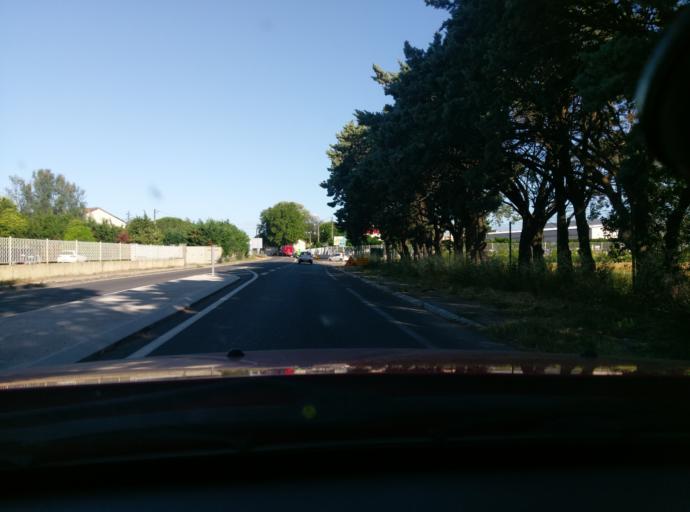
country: FR
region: Languedoc-Roussillon
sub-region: Departement du Gard
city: Uzes
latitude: 43.9921
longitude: 4.4276
